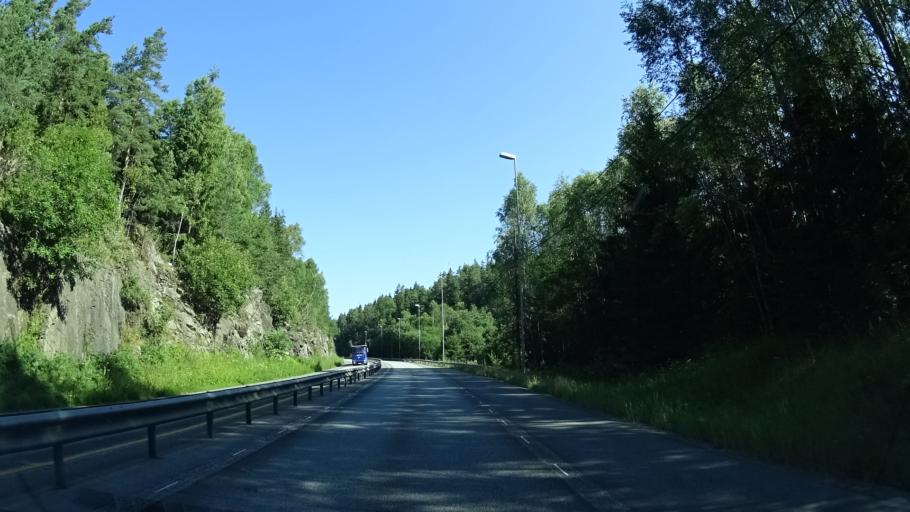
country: NO
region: Akershus
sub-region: Oppegard
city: Kolbotn
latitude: 59.7634
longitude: 10.7755
